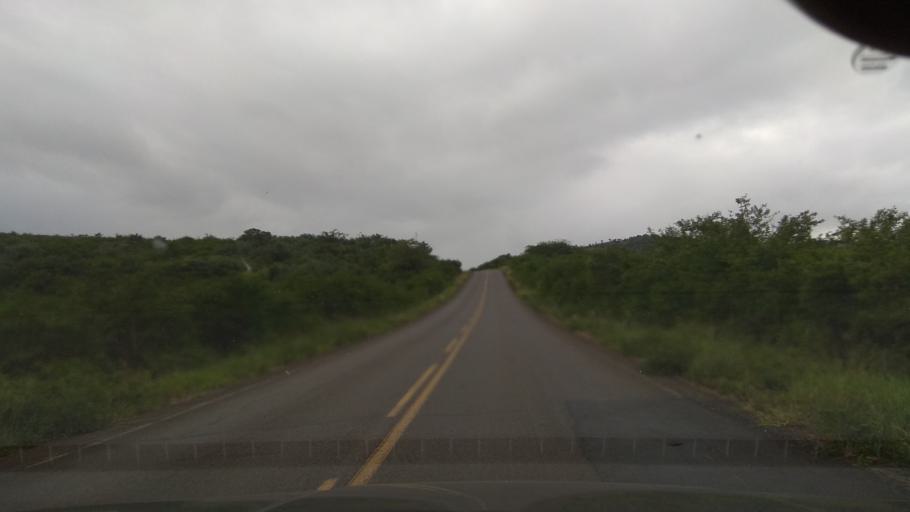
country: BR
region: Bahia
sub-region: Santa Ines
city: Santa Ines
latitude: -13.2710
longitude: -39.8021
